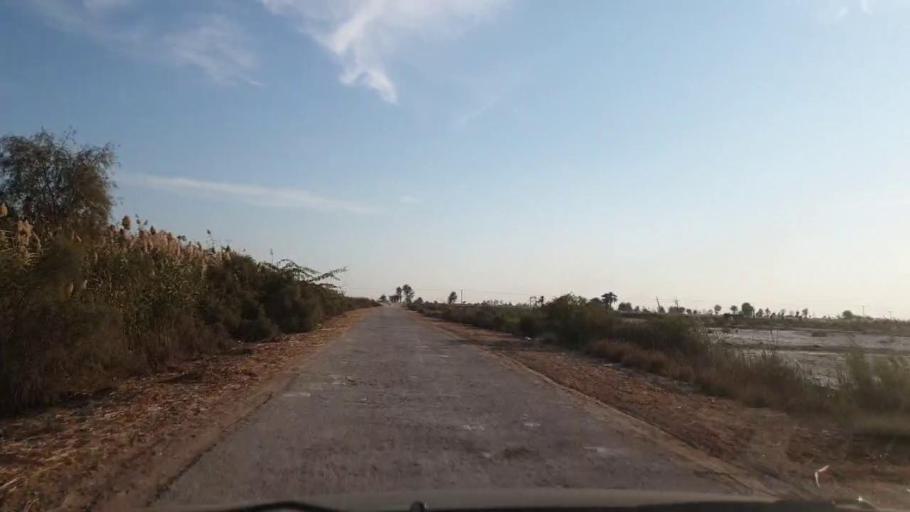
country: PK
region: Sindh
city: Khadro
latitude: 26.1803
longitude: 68.7501
